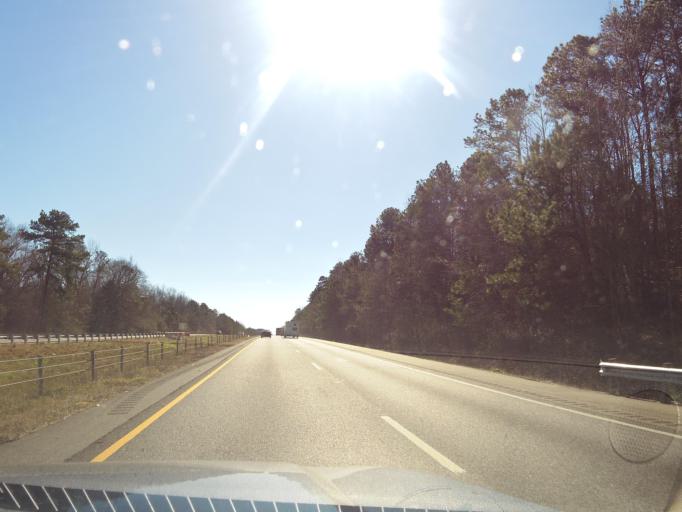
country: US
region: Alabama
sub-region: Autauga County
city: Marbury
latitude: 32.7212
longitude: -86.5330
